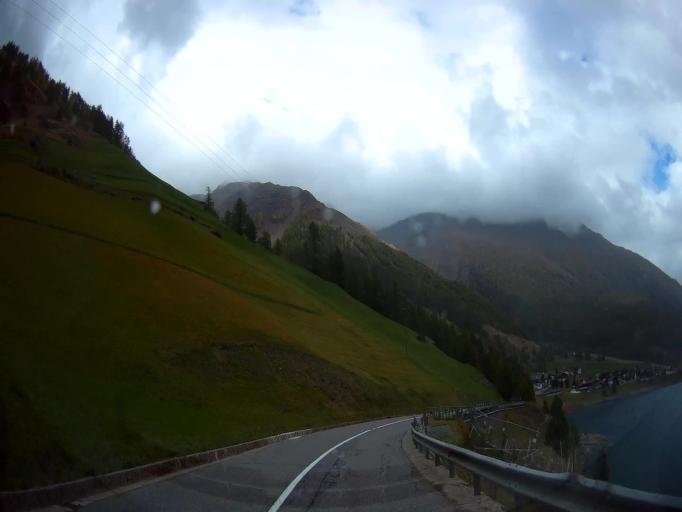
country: IT
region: Trentino-Alto Adige
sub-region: Bolzano
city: Senales
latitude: 46.7388
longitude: 10.8390
